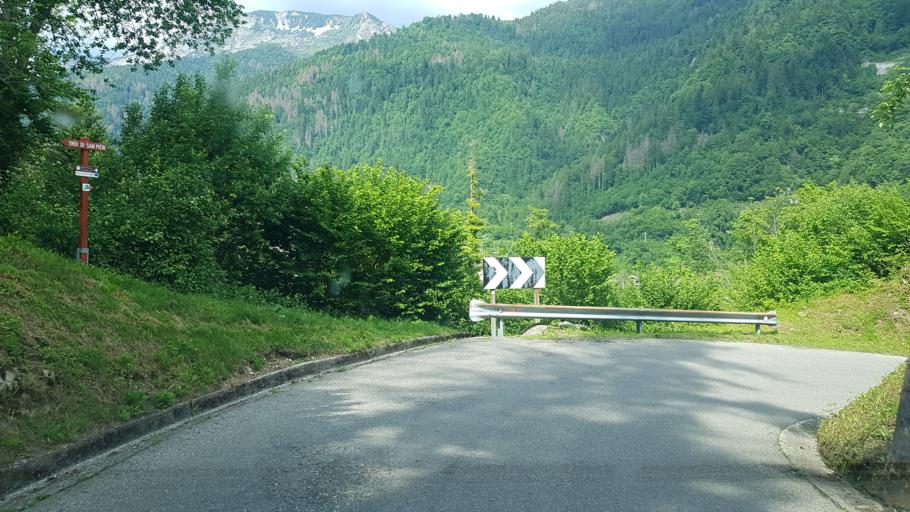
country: IT
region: Friuli Venezia Giulia
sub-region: Provincia di Udine
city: Zuglio
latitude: 46.4661
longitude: 13.0210
